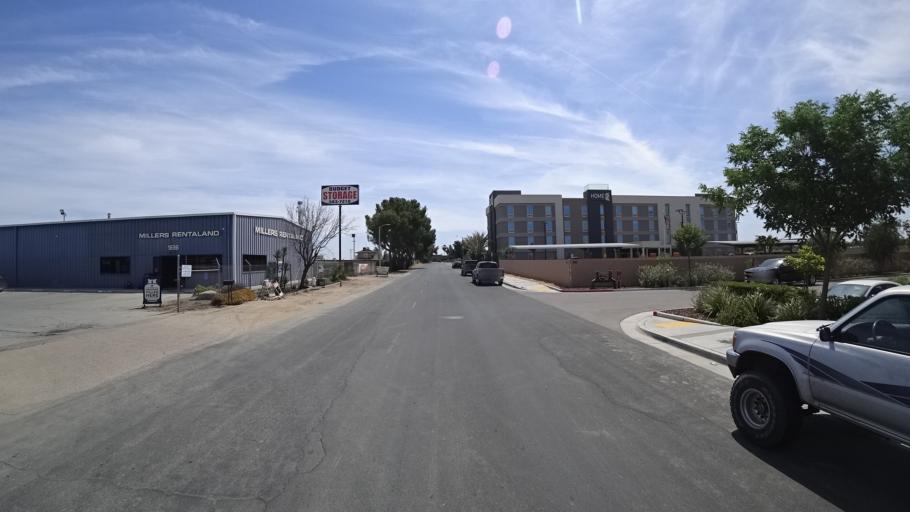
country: US
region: California
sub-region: Kings County
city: Hanford
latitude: 36.3202
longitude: -119.6717
